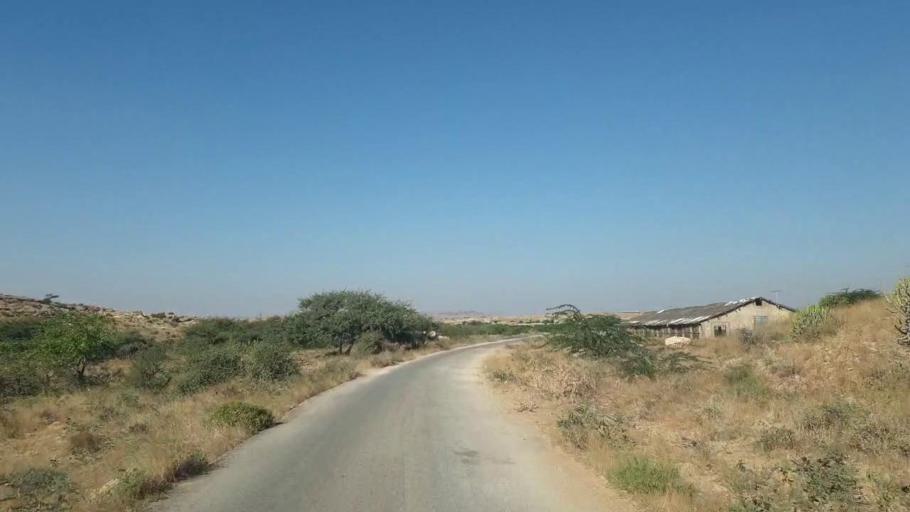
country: PK
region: Sindh
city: Gharo
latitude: 25.0850
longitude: 67.5362
